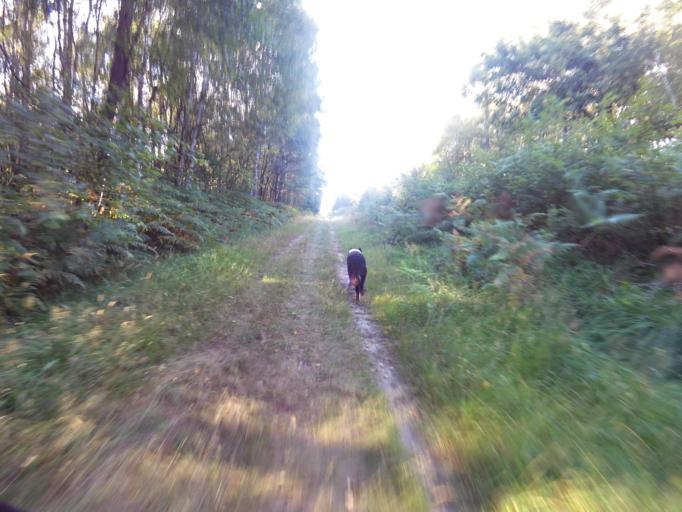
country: FR
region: Brittany
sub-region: Departement du Morbihan
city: Molac
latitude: 47.7476
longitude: -2.4302
